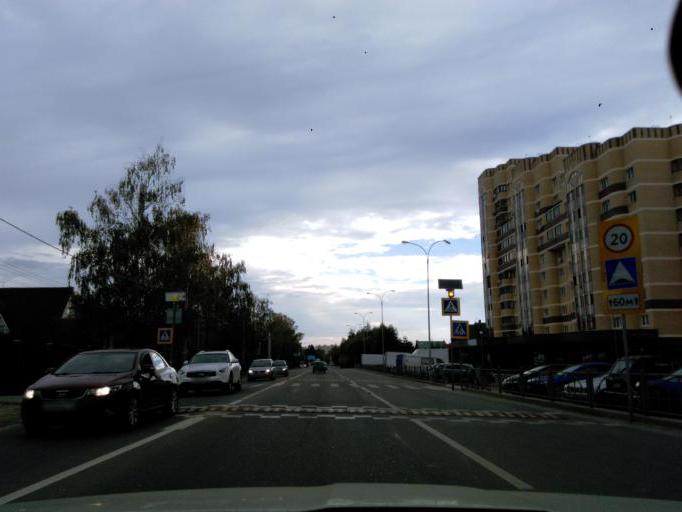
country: RU
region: Moskovskaya
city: Andreyevka
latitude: 55.9810
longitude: 37.1290
